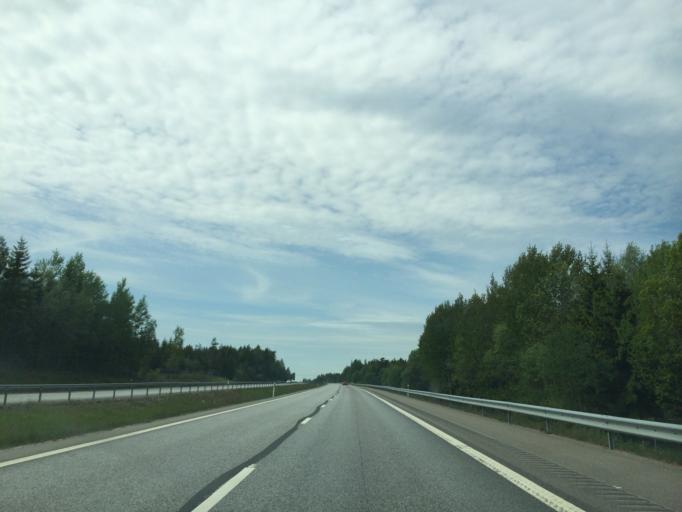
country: SE
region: Soedermanland
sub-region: Trosa Kommun
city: Vagnharad
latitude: 58.9597
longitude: 17.4637
